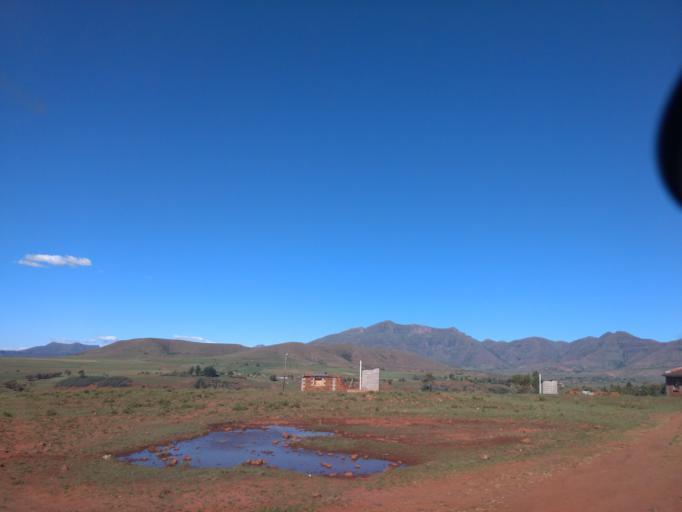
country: LS
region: Berea
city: Teyateyaneng
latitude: -29.3679
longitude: 27.7867
